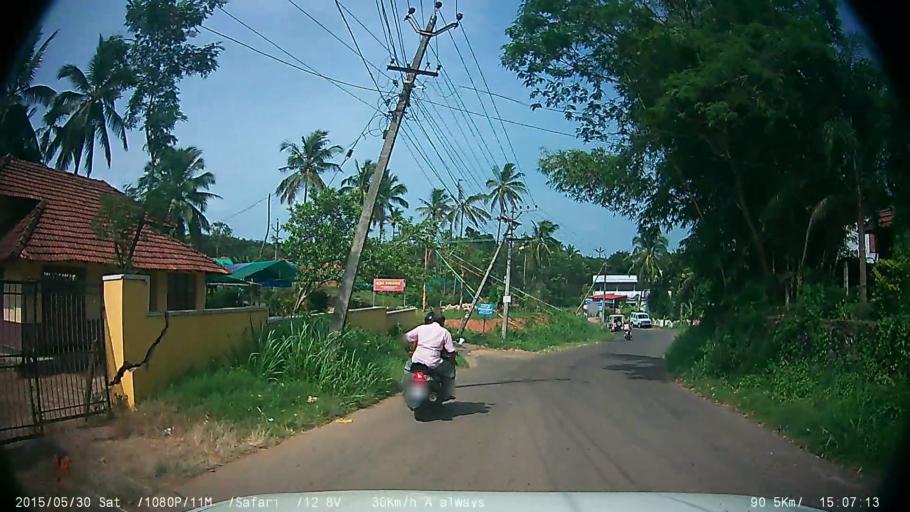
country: IN
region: Kerala
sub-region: Wayanad
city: Panamaram
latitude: 11.8017
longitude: 76.0136
